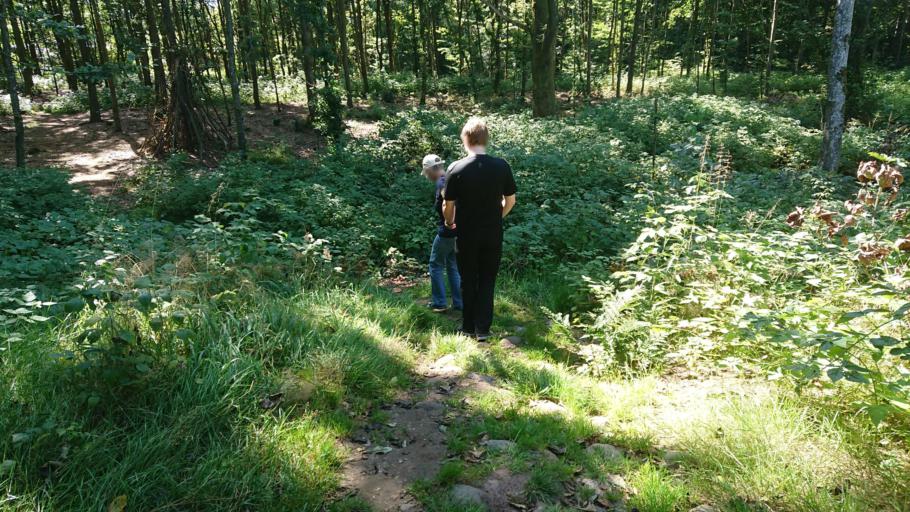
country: DK
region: Central Jutland
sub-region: Skanderborg Kommune
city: Ry
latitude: 55.9928
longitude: 9.7956
